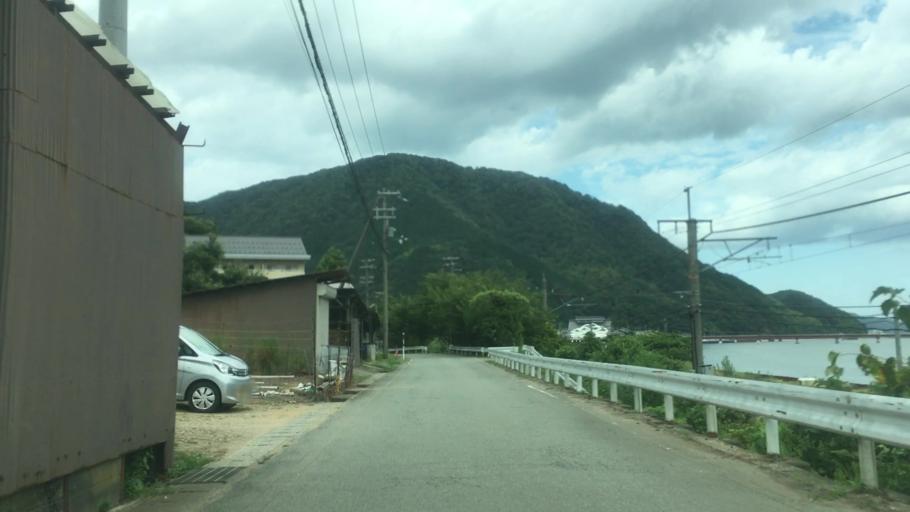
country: JP
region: Hyogo
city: Toyooka
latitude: 35.6005
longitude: 134.8014
